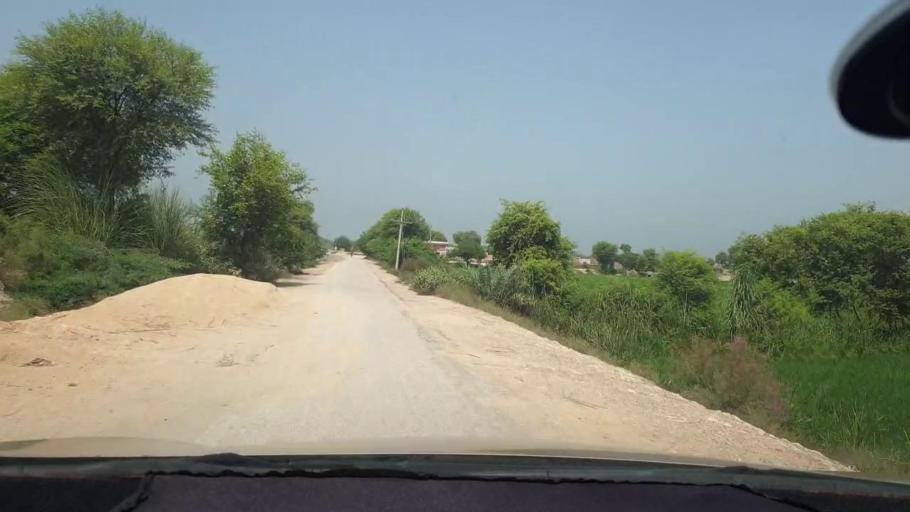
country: PK
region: Sindh
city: Kambar
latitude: 27.6586
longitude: 67.8802
